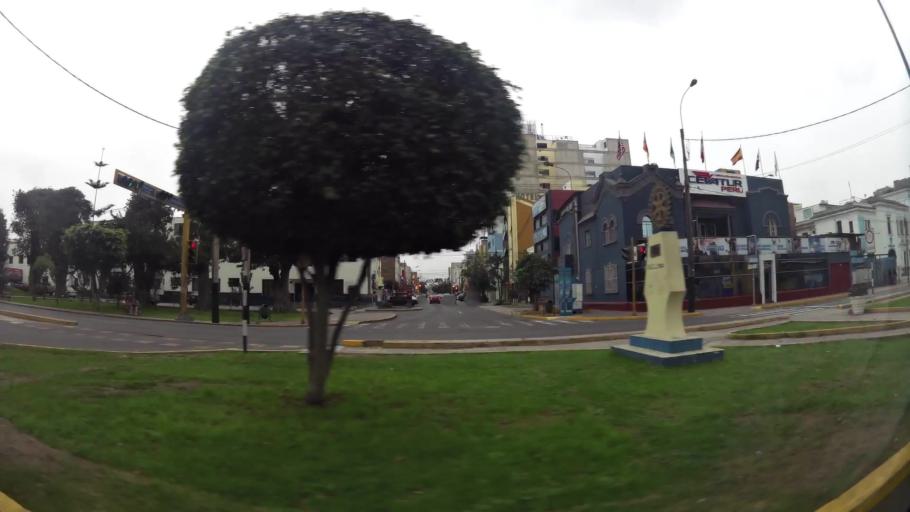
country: PE
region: Lima
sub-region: Lima
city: San Isidro
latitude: -12.0892
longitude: -77.0339
